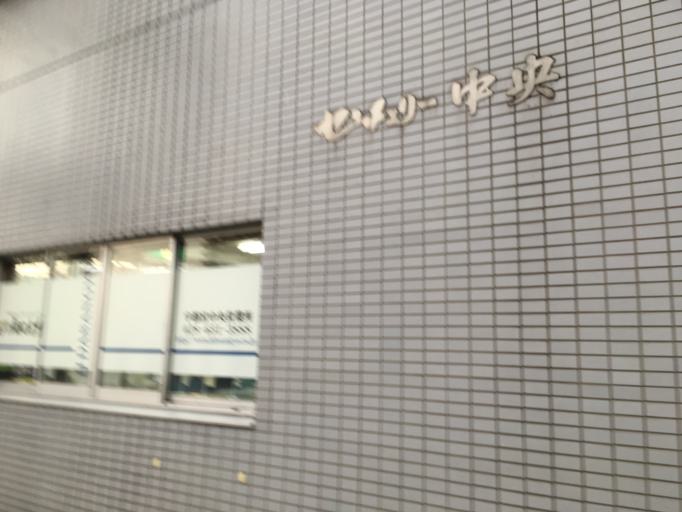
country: JP
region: Tochigi
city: Utsunomiya-shi
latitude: 36.5560
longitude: 139.8851
